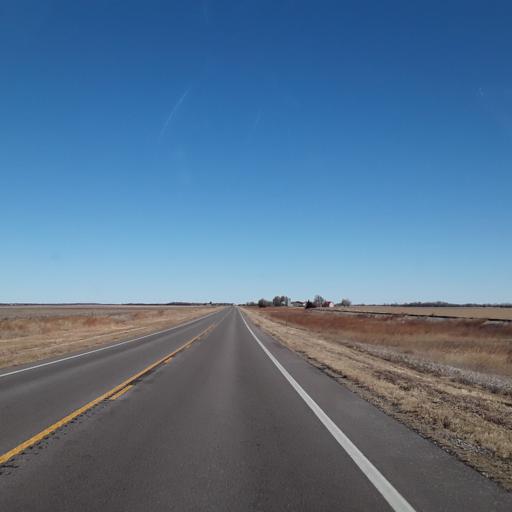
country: US
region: Kansas
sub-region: Pawnee County
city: Larned
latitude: 38.0907
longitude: -99.2214
